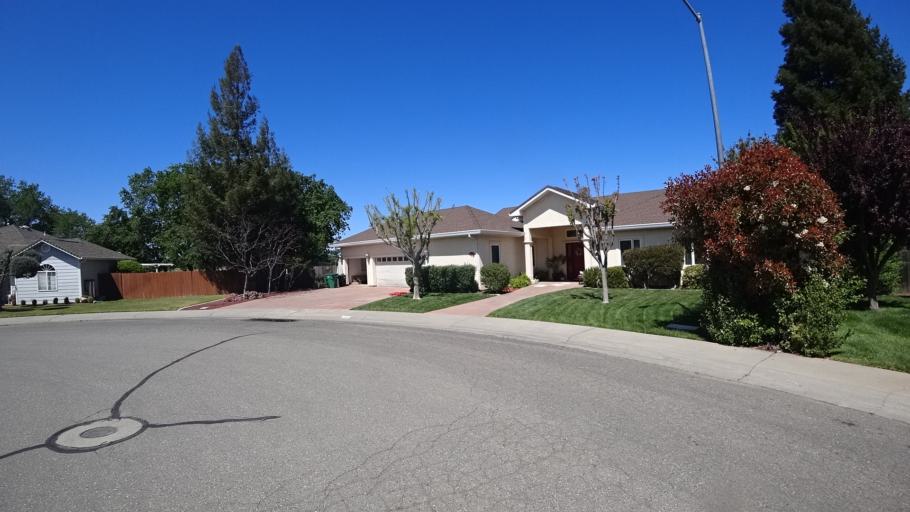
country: US
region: California
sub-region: Glenn County
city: Orland
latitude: 39.7548
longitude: -122.1801
